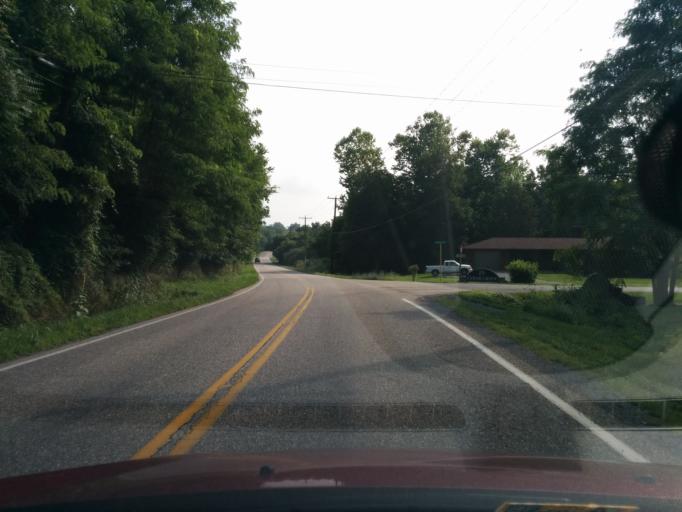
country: US
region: Virginia
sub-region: City of Lexington
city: Lexington
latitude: 37.7638
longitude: -79.4598
